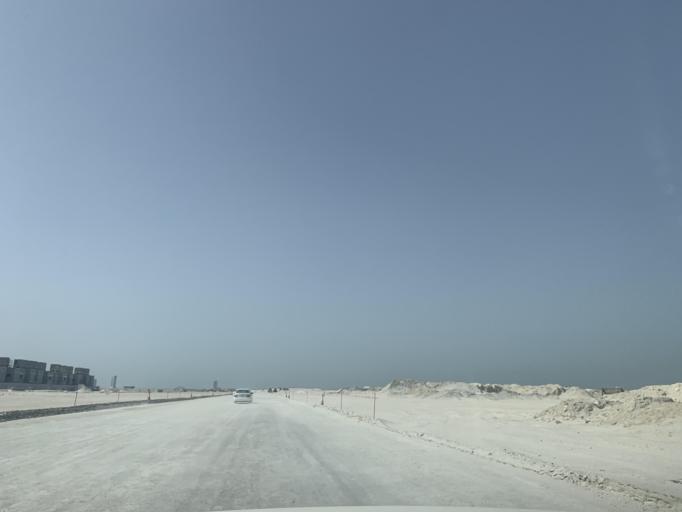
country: BH
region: Northern
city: Sitrah
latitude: 26.1643
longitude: 50.6362
